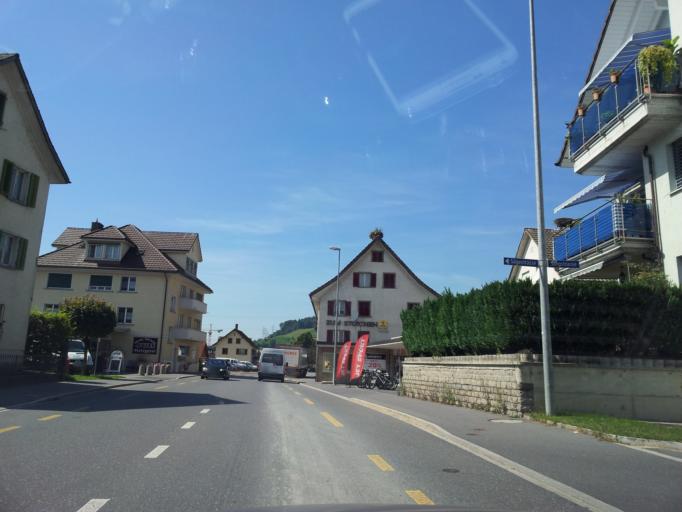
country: CH
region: Saint Gallen
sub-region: Wahlkreis See-Gaster
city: Uznach
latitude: 47.2275
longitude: 8.9766
